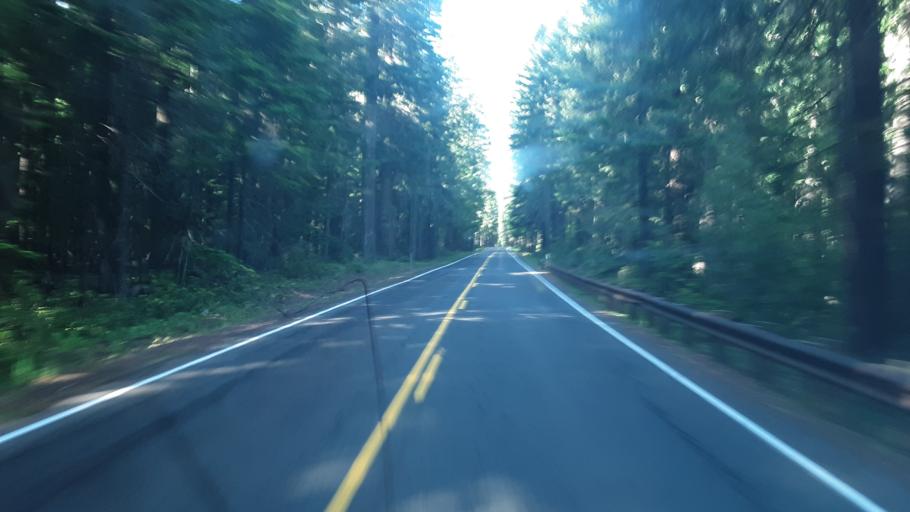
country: US
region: Oregon
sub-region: Jackson County
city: Shady Cove
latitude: 42.9478
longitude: -122.4115
